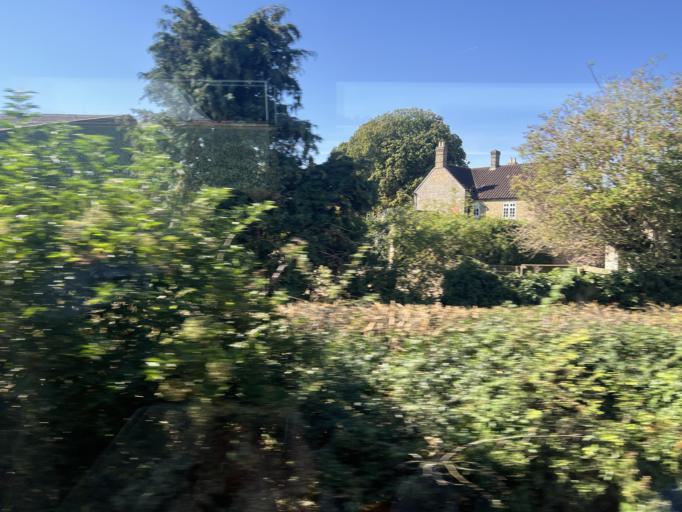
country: GB
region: England
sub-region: Lincolnshire
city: Sleaford
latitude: 52.9904
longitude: -0.3628
